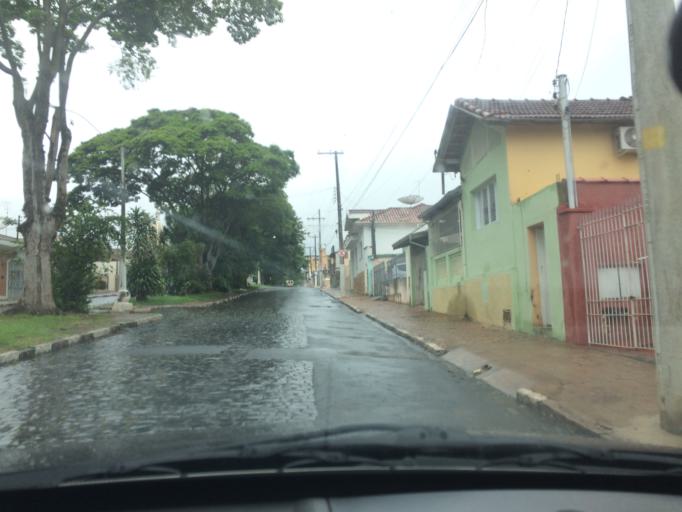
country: BR
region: Sao Paulo
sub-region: Casa Branca
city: Casa Branca
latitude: -21.7727
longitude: -47.0890
